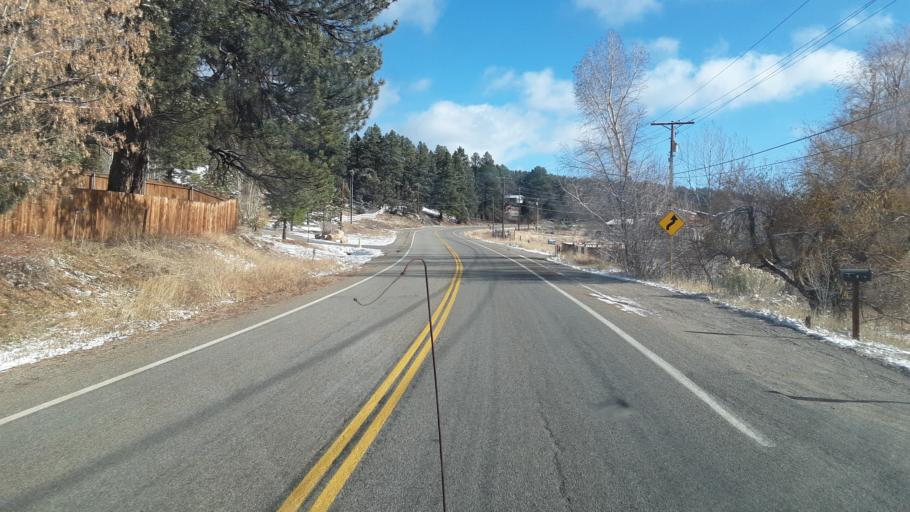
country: US
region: Colorado
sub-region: La Plata County
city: Durango
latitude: 37.3086
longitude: -107.8157
